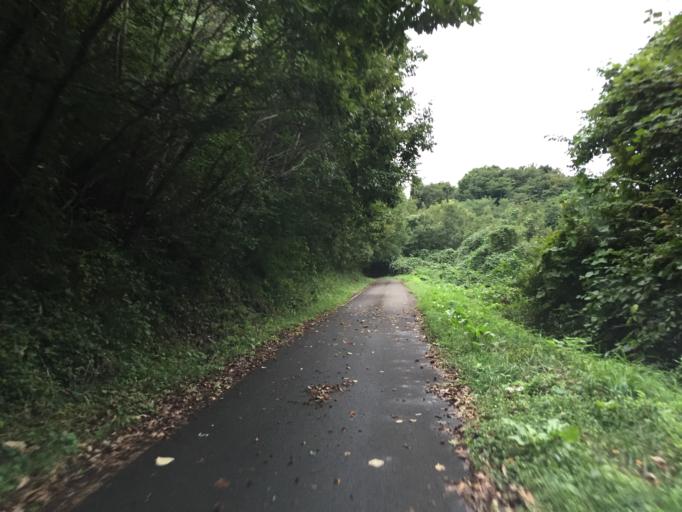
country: JP
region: Fukushima
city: Hobaramachi
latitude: 37.7669
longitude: 140.5276
